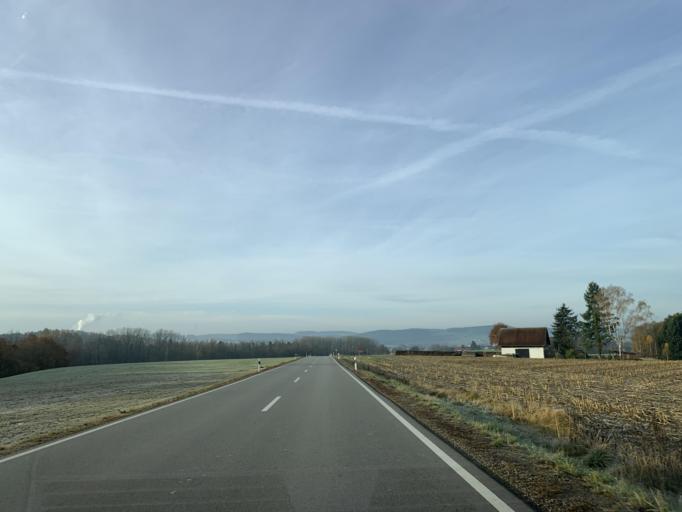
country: DE
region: Bavaria
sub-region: Upper Palatinate
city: Neunburg vorm Wald
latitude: 49.3549
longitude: 12.4142
